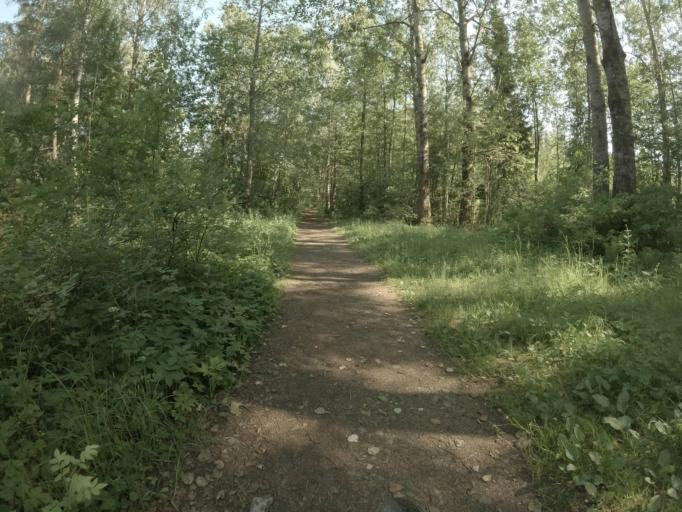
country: RU
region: Leningrad
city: Yakovlevo
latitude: 60.4650
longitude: 29.2794
